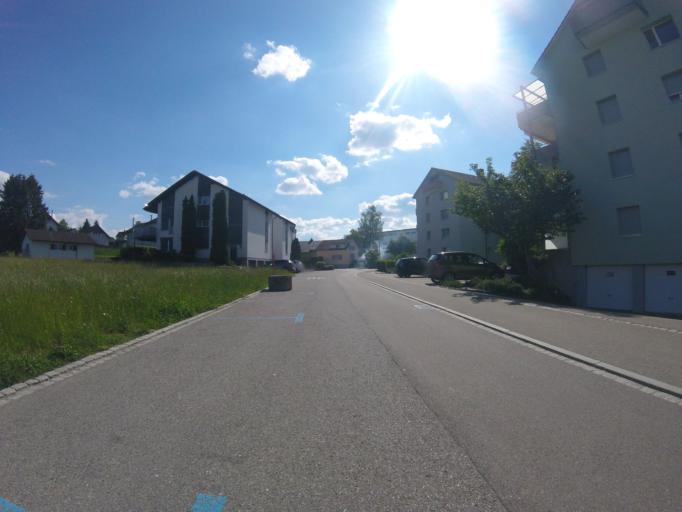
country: CH
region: Saint Gallen
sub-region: Wahlkreis St. Gallen
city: Gossau
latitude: 47.4116
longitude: 9.2438
